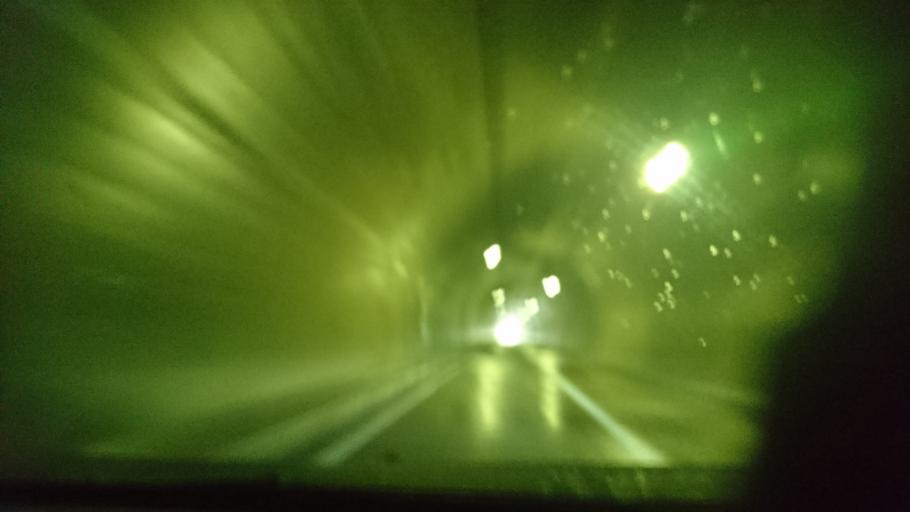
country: JP
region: Akita
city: Yuzawa
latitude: 39.1502
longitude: 140.7640
